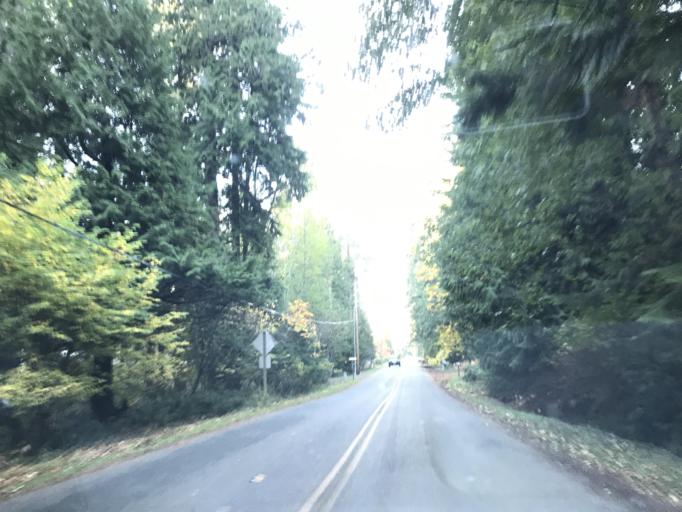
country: US
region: Washington
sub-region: Whatcom County
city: Geneva
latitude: 48.7428
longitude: -122.4153
